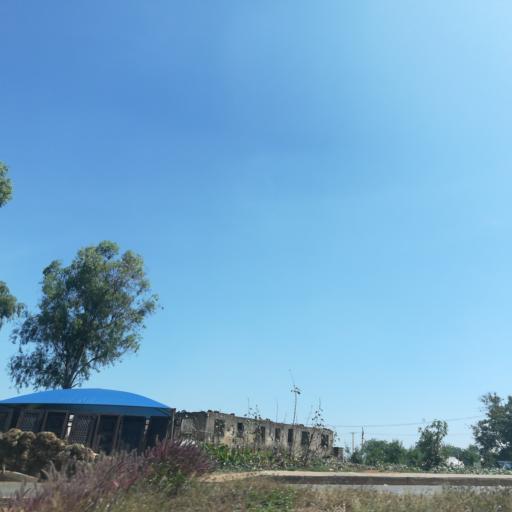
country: NG
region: Plateau
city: Bukuru
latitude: 9.7825
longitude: 8.8601
